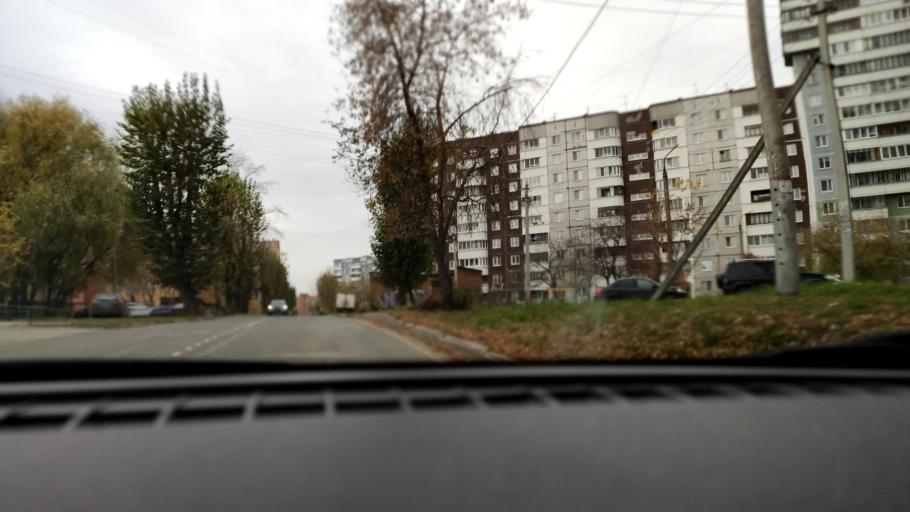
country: RU
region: Perm
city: Perm
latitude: 58.0324
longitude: 56.3119
